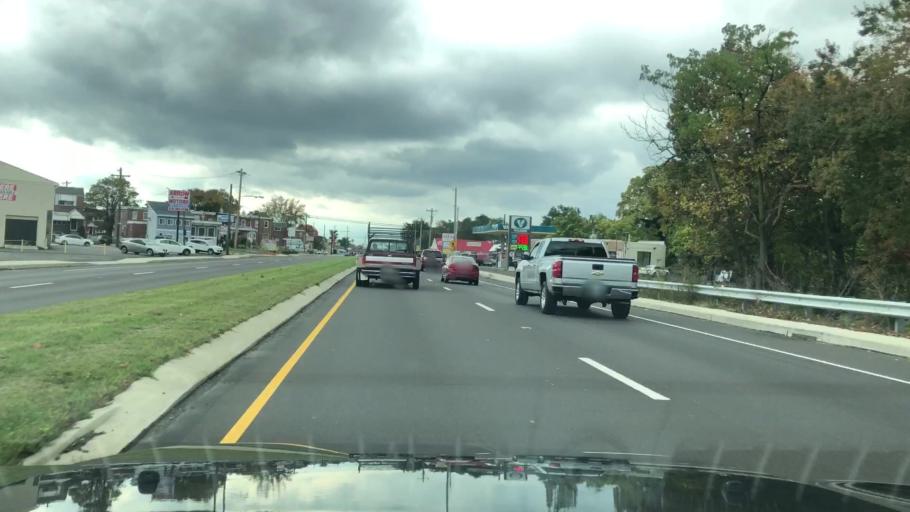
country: US
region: Pennsylvania
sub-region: Bucks County
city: Bristol
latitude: 40.1090
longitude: -74.8566
